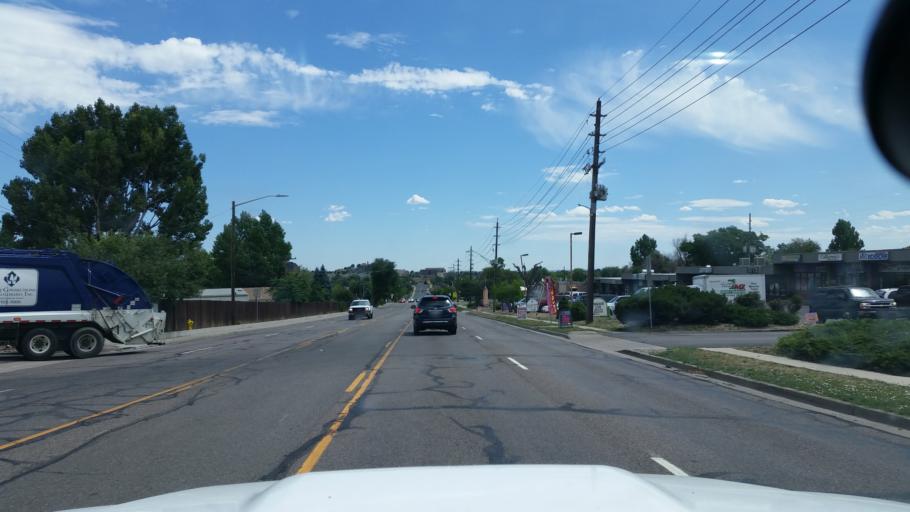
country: US
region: Colorado
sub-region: Adams County
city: Federal Heights
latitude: 39.8635
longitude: -105.0094
